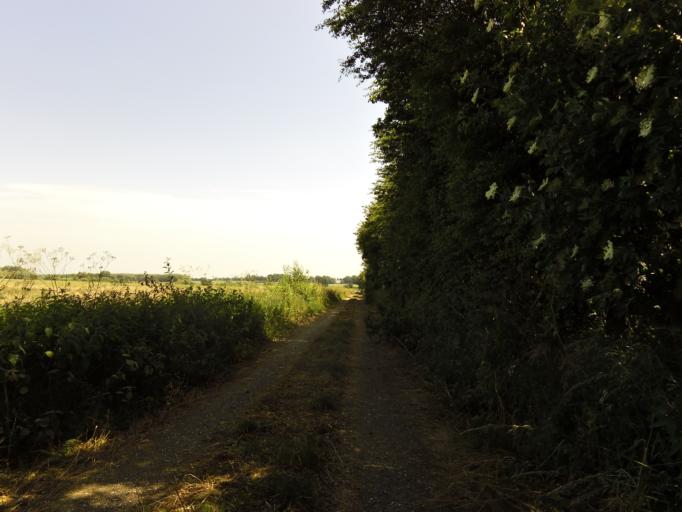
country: DK
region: South Denmark
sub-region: Haderslev Kommune
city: Vojens
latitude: 55.1586
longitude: 9.2367
